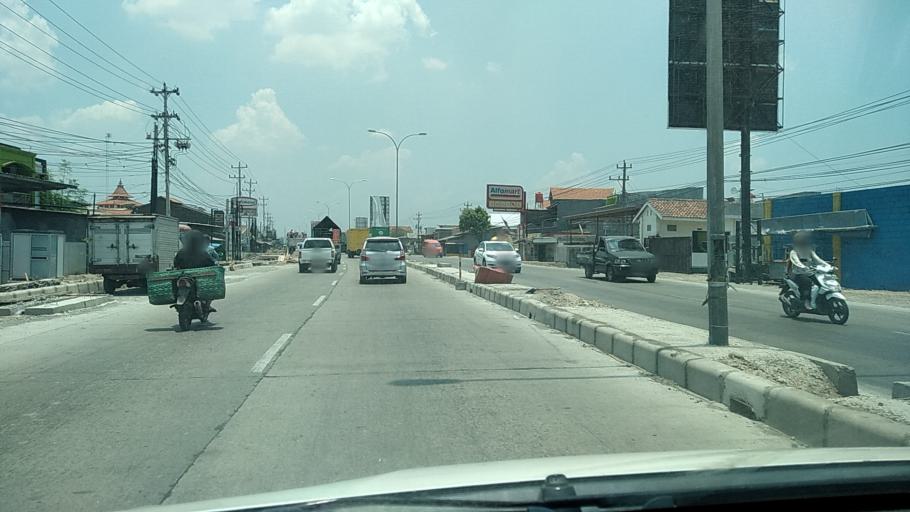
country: ID
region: Central Java
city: Semarang
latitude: -6.9556
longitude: 110.4683
